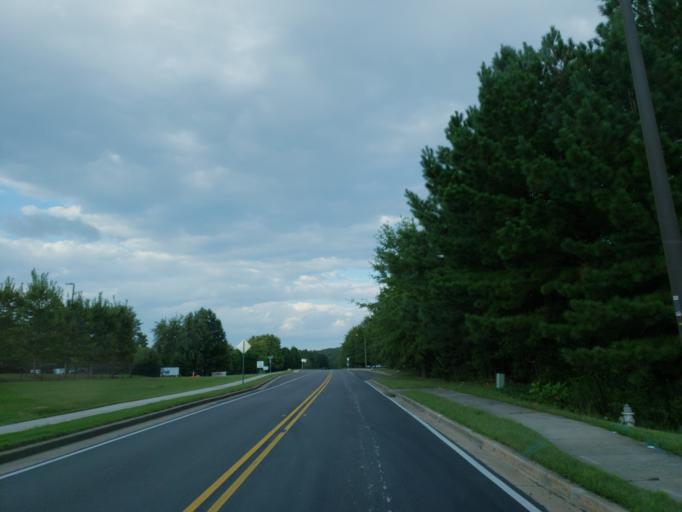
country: US
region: Georgia
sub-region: Cobb County
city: Mableton
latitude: 33.7869
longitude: -84.5272
